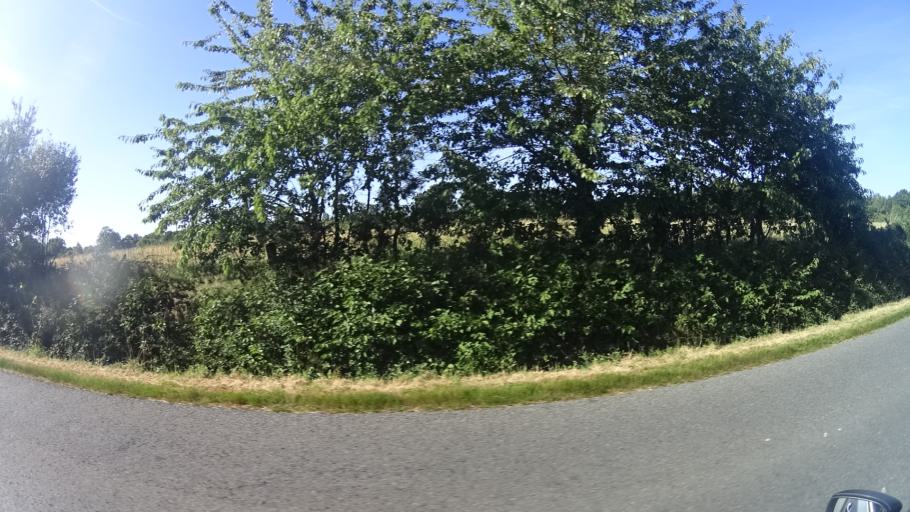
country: FR
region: Brittany
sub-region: Departement d'Ille-et-Vilaine
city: Langon
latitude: 47.7396
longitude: -1.7933
